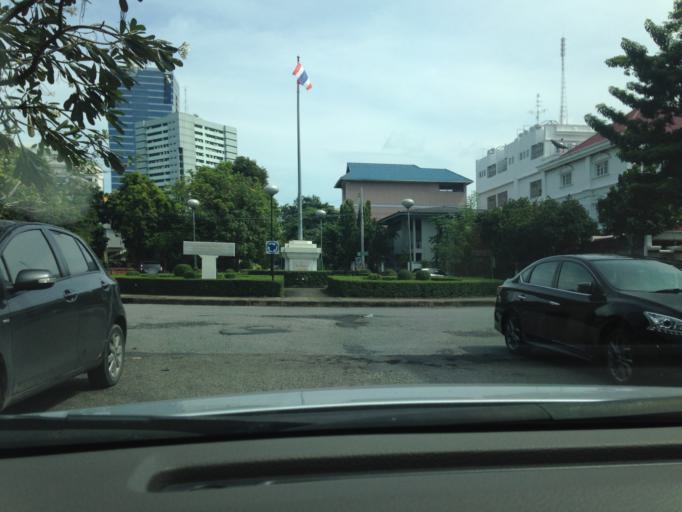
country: TH
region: Bangkok
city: Phaya Thai
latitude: 13.7857
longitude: 100.5365
